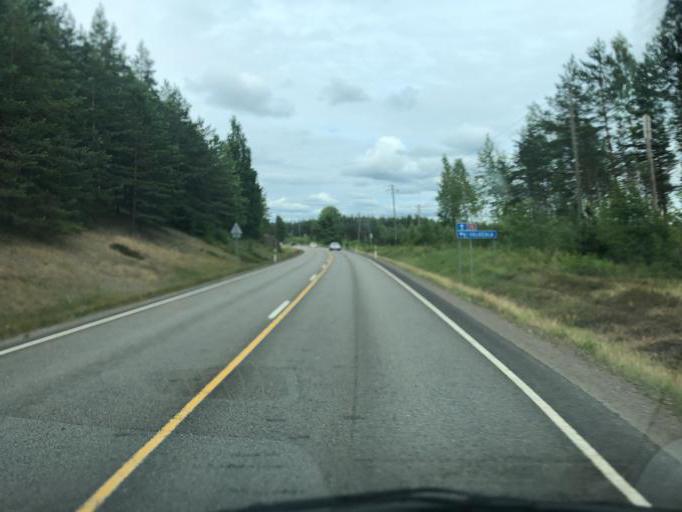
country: FI
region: Kymenlaakso
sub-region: Kouvola
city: Kouvola
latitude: 60.9371
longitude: 26.8199
